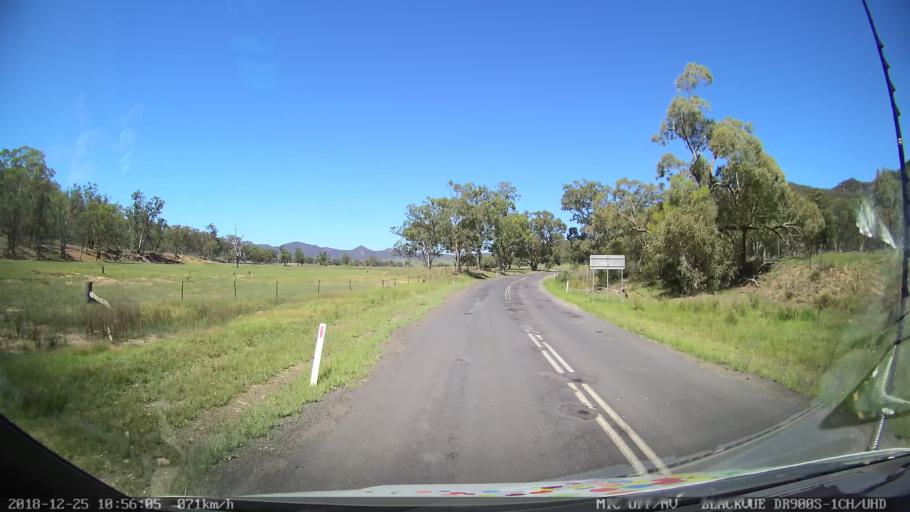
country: AU
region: New South Wales
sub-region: Upper Hunter Shire
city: Merriwa
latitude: -32.3998
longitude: 150.2665
